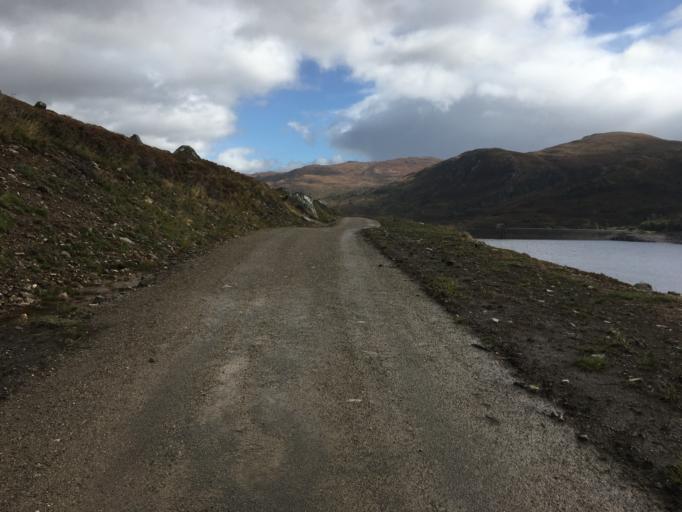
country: GB
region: Scotland
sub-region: Highland
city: Spean Bridge
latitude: 57.3399
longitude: -4.9673
